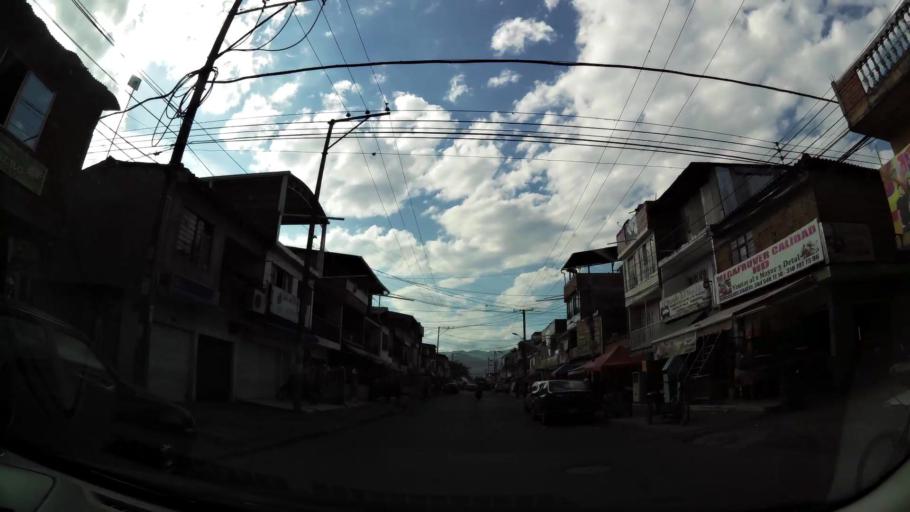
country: CO
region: Valle del Cauca
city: Cali
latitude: 3.4200
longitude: -76.4983
